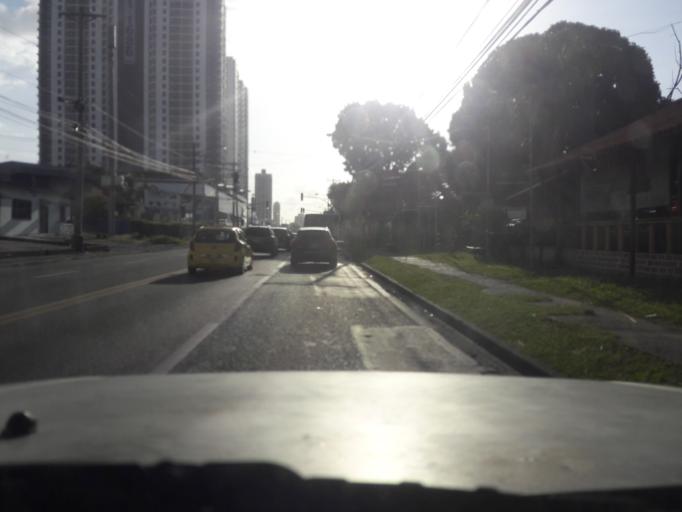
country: PA
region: Panama
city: Panama
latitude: 9.0178
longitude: -79.4941
